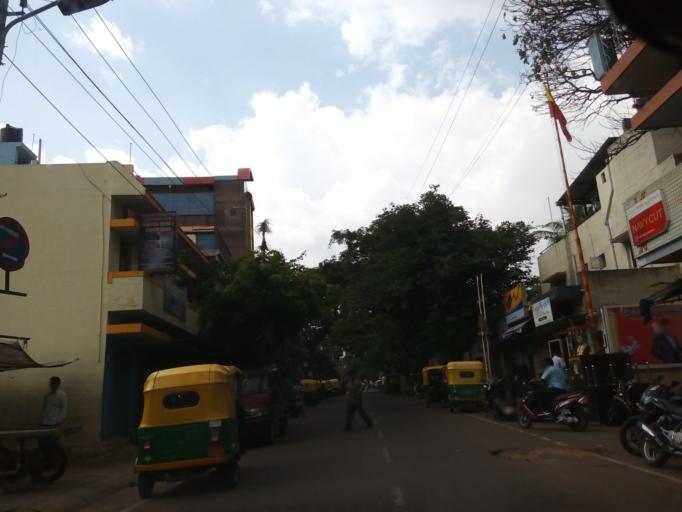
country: IN
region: Karnataka
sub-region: Bangalore Urban
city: Bangalore
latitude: 13.0240
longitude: 77.5596
